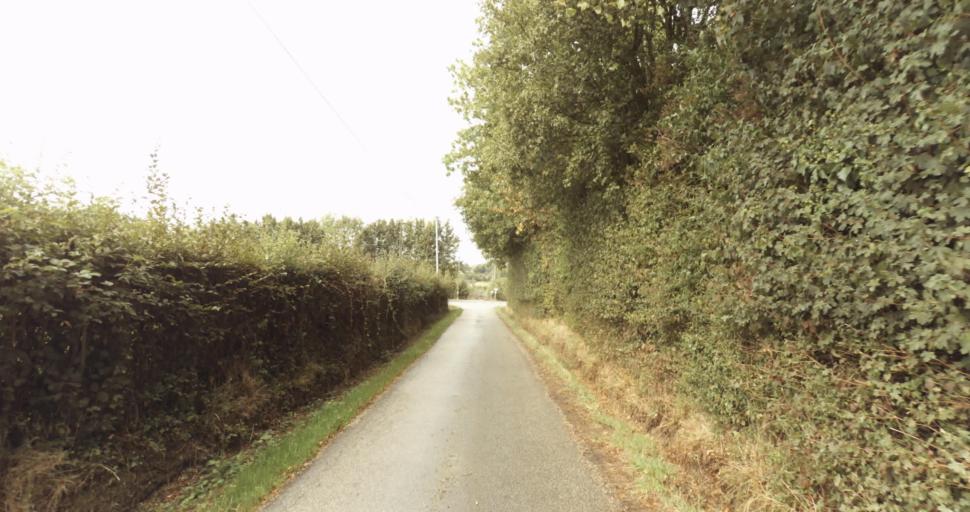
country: FR
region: Lower Normandy
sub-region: Departement de l'Orne
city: Sainte-Gauburge-Sainte-Colombe
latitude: 48.7125
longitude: 0.4155
